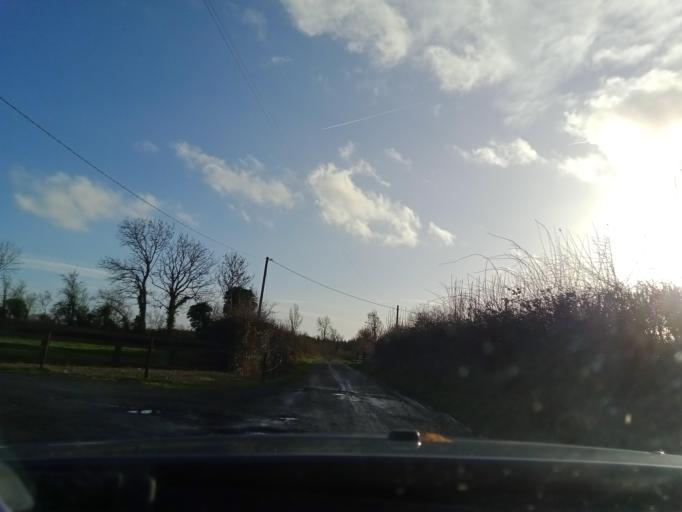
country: IE
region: Leinster
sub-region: Kilkenny
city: Callan
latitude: 52.5207
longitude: -7.4009
